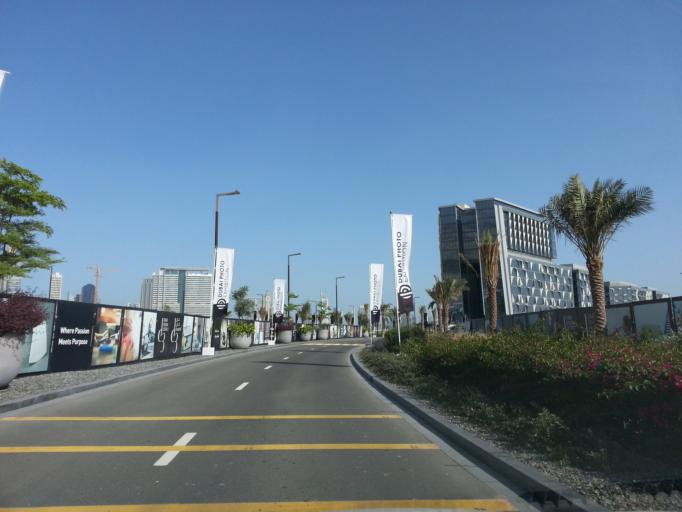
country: AE
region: Dubai
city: Dubai
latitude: 25.1843
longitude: 55.2973
